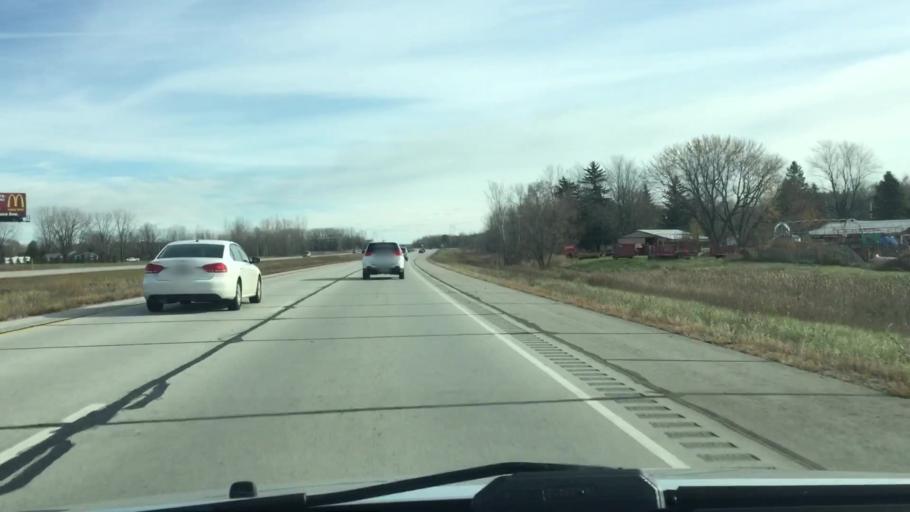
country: US
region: Wisconsin
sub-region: Brown County
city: Oneida
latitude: 44.5878
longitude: -88.1980
